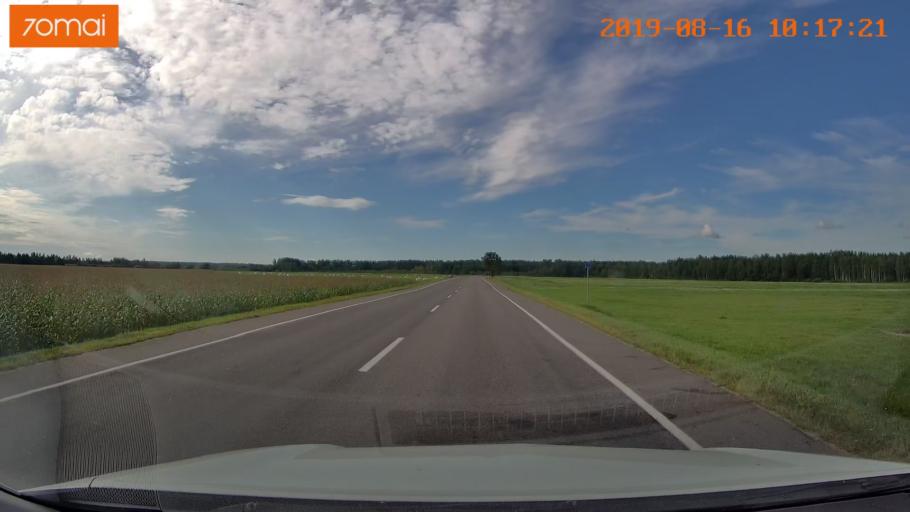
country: BY
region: Mogilev
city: Asipovichy
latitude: 53.3119
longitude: 28.7125
